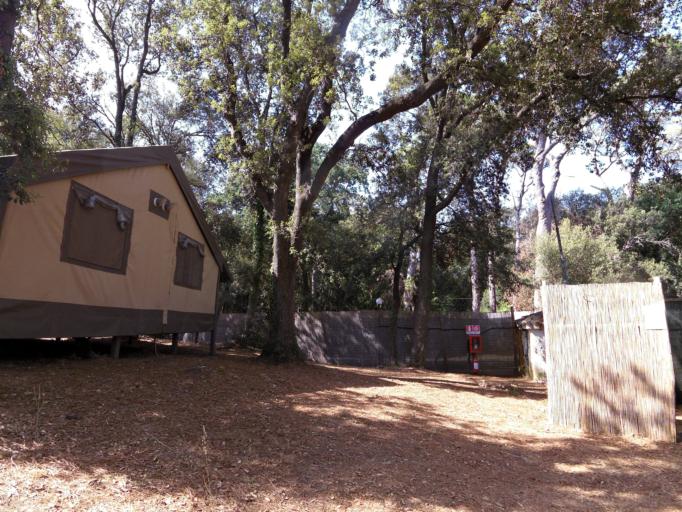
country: IT
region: Tuscany
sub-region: Provincia di Livorno
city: Donoratico
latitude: 43.1551
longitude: 10.5455
